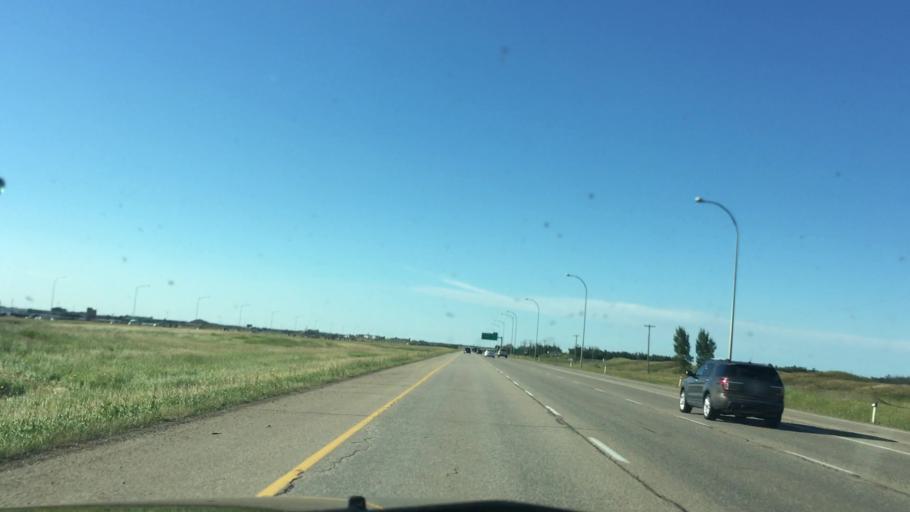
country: CA
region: Alberta
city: Leduc
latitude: 53.3338
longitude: -113.5498
